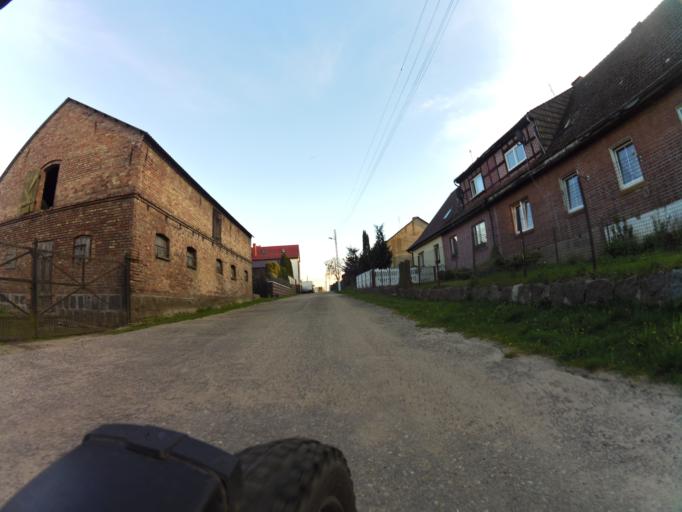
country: PL
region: West Pomeranian Voivodeship
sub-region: Powiat lobeski
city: Lobez
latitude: 53.7010
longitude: 15.6467
